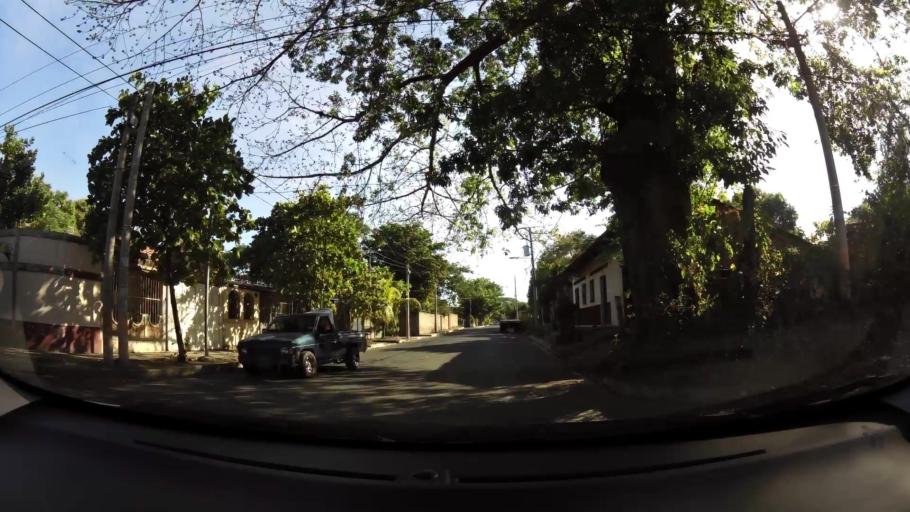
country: SV
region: San Miguel
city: San Miguel
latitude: 13.4781
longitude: -88.1896
